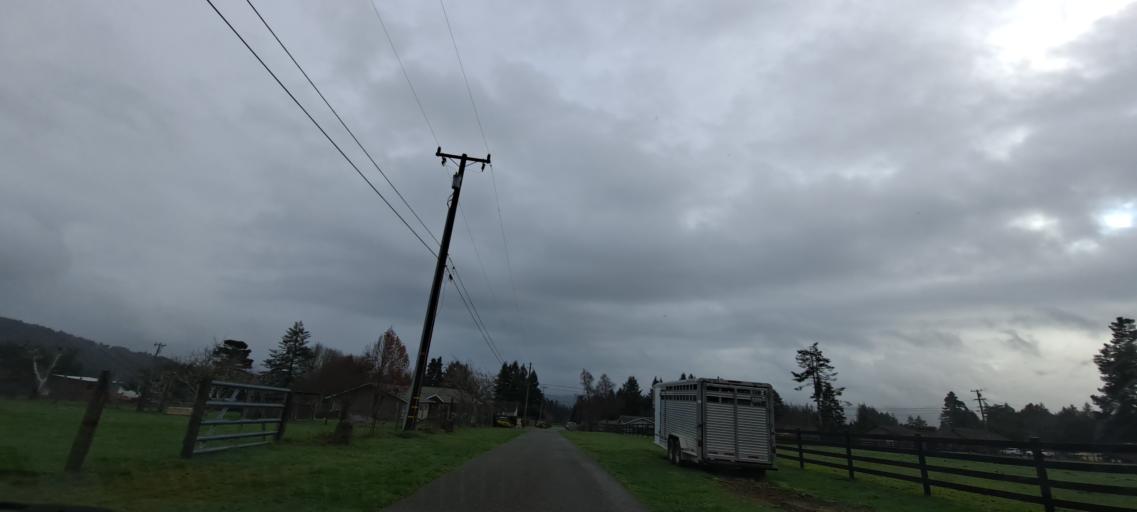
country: US
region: California
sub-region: Humboldt County
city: Fortuna
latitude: 40.6056
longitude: -124.1364
